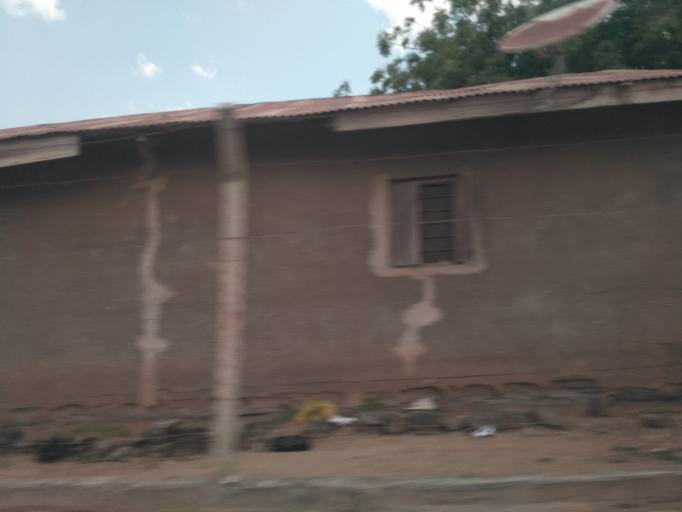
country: TZ
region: Dar es Salaam
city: Dar es Salaam
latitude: -6.8263
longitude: 39.3124
